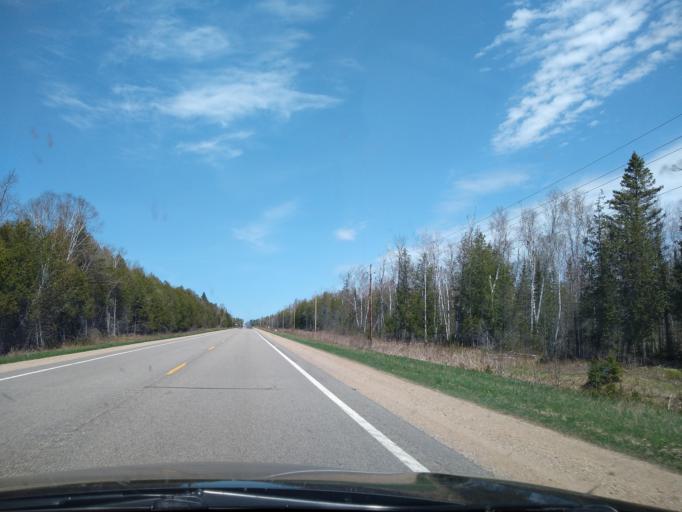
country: US
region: Michigan
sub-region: Delta County
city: Gladstone
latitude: 46.1075
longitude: -86.9806
